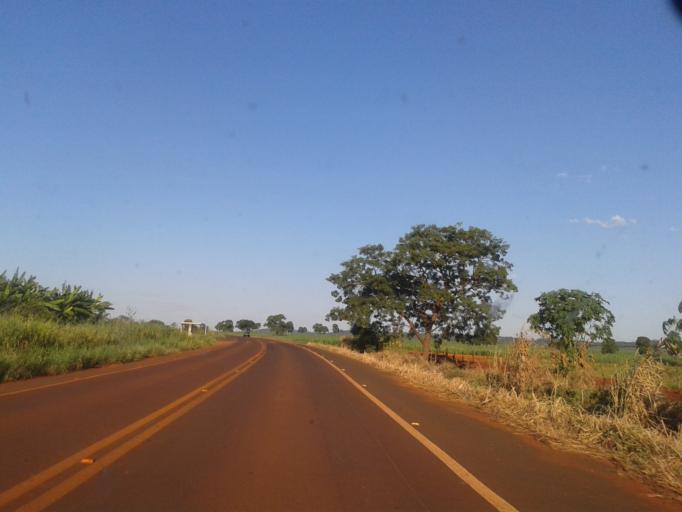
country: BR
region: Minas Gerais
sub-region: Capinopolis
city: Capinopolis
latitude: -18.7119
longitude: -49.8439
